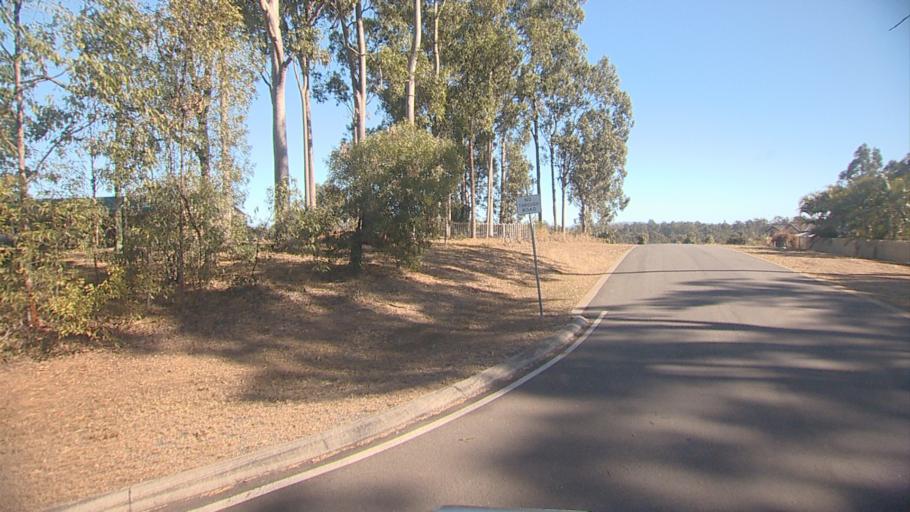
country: AU
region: Queensland
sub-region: Logan
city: Cedar Vale
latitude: -27.8676
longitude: 153.0038
